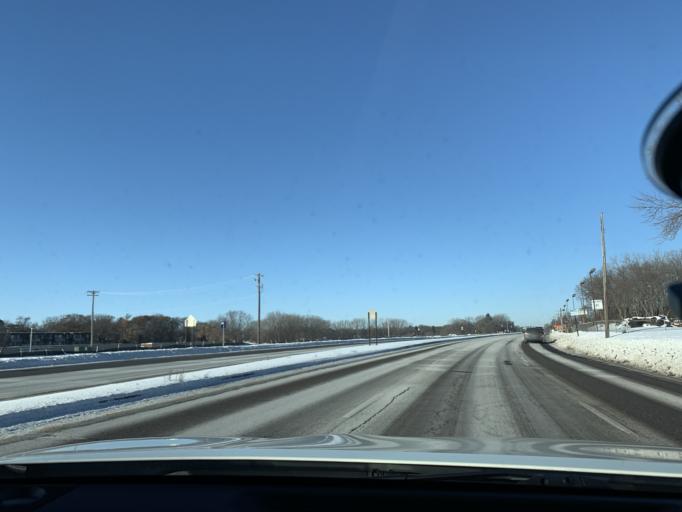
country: US
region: Minnesota
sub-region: Anoka County
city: Coon Rapids
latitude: 45.1520
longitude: -93.3009
